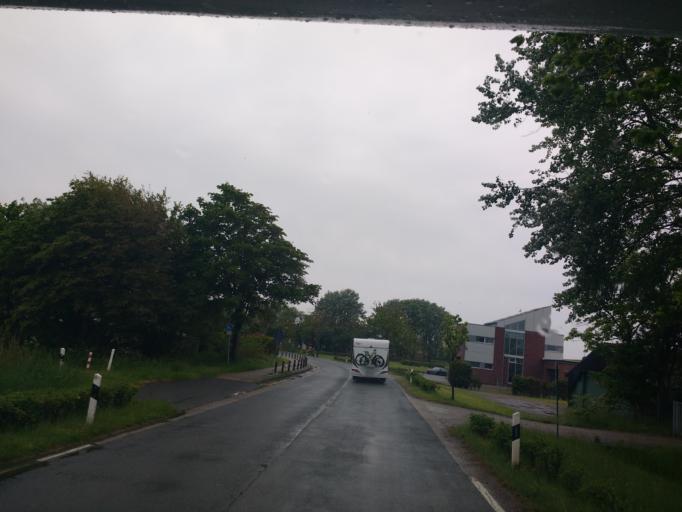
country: DE
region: Lower Saxony
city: Neuharlingersiel
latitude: 53.6995
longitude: 7.7081
